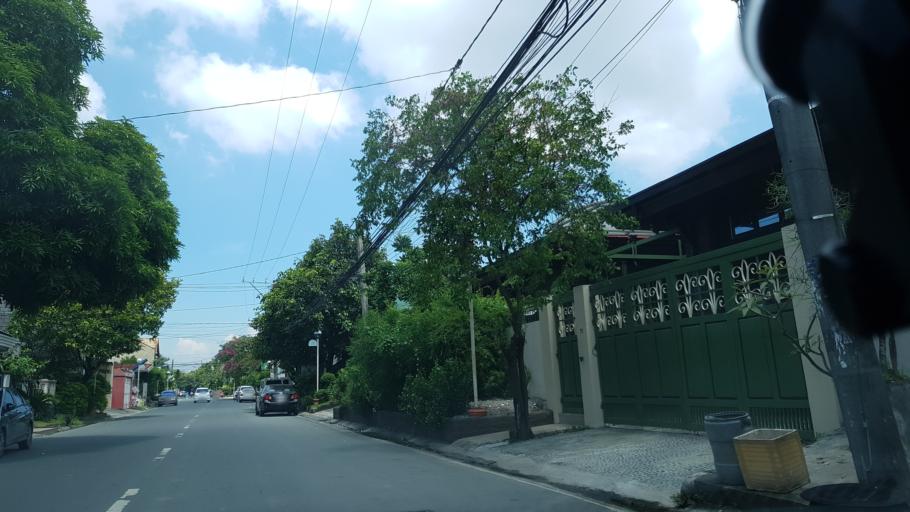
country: PH
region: Calabarzon
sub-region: Province of Rizal
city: Las Pinas
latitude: 14.4360
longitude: 120.9845
